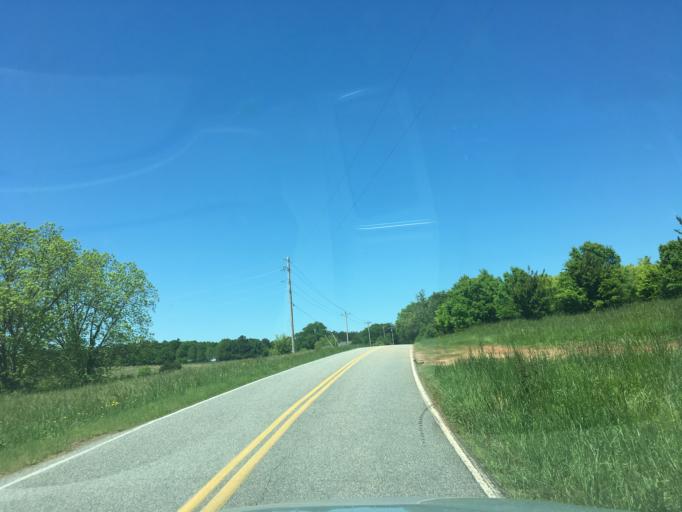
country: US
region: South Carolina
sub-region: Spartanburg County
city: Duncan
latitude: 34.8725
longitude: -82.1780
